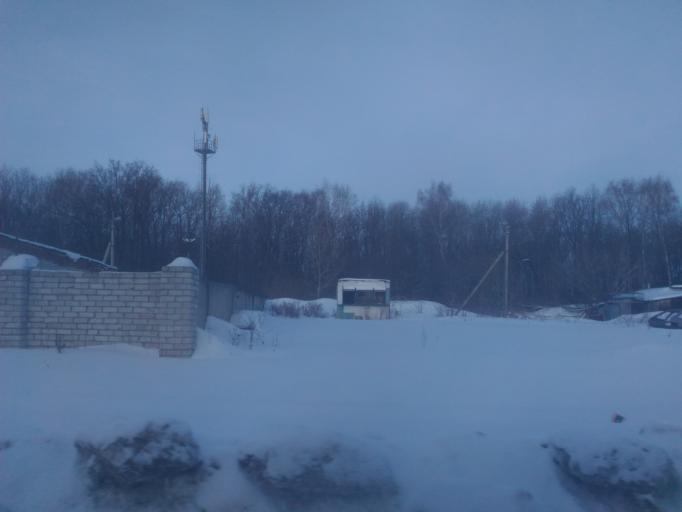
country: RU
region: Ulyanovsk
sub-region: Ulyanovskiy Rayon
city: Ulyanovsk
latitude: 54.3661
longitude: 48.3506
